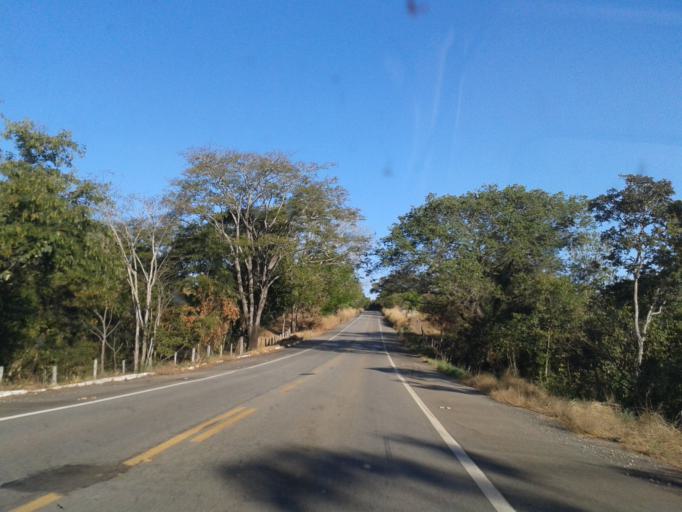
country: BR
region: Goias
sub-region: Itapuranga
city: Itapuranga
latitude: -15.6091
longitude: -50.2493
